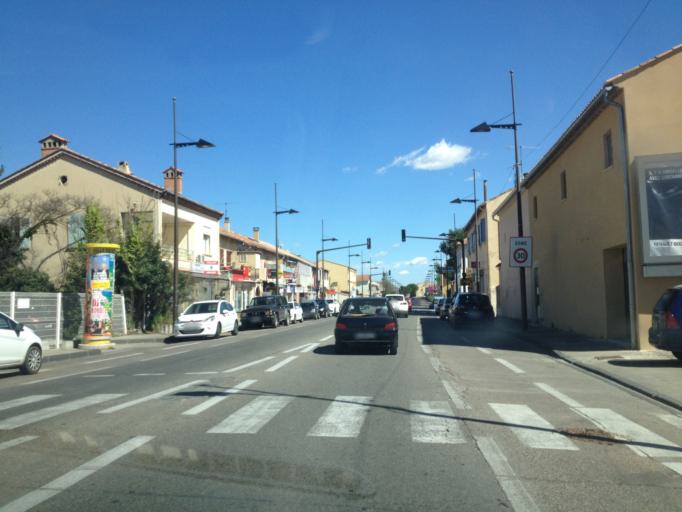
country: FR
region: Provence-Alpes-Cote d'Azur
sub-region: Departement du Vaucluse
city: Le Pontet
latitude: 43.9555
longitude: 4.8422
